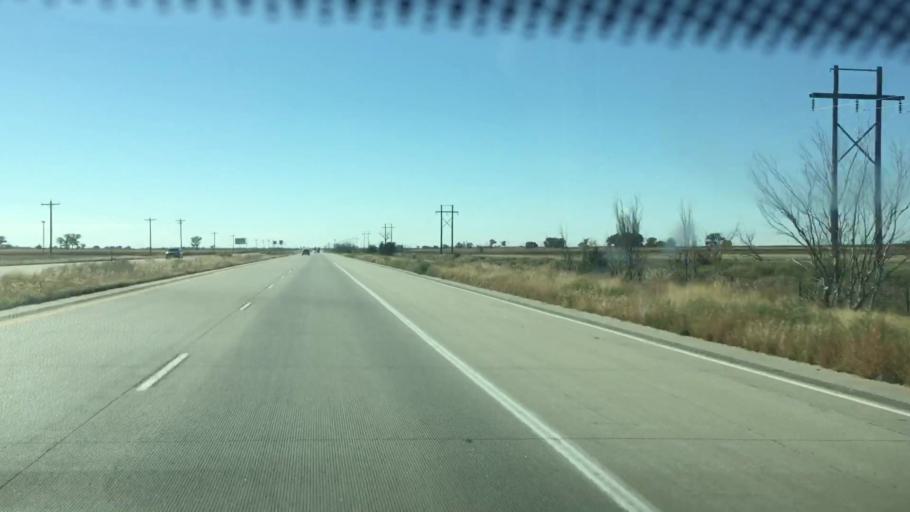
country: US
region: Colorado
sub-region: Prowers County
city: Lamar
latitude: 38.1107
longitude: -102.6703
